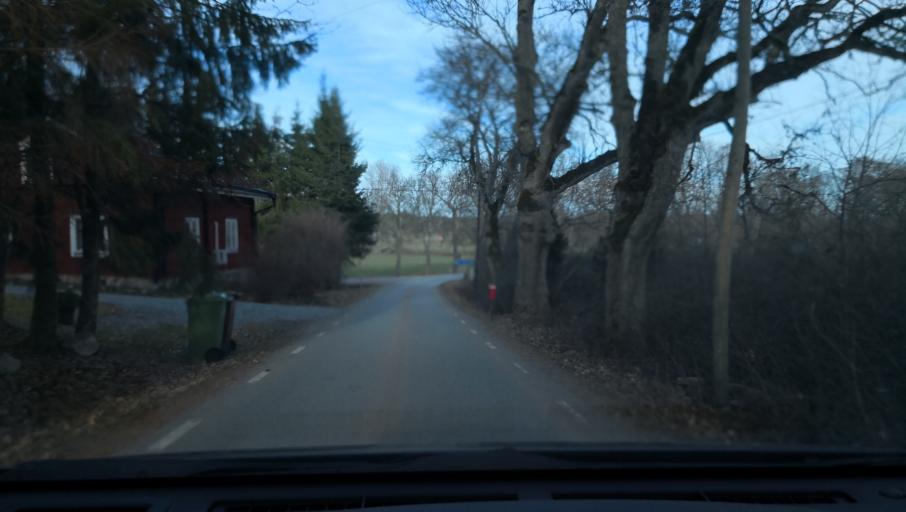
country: SE
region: Uppsala
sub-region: Enkopings Kommun
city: Grillby
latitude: 59.5424
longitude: 17.1949
